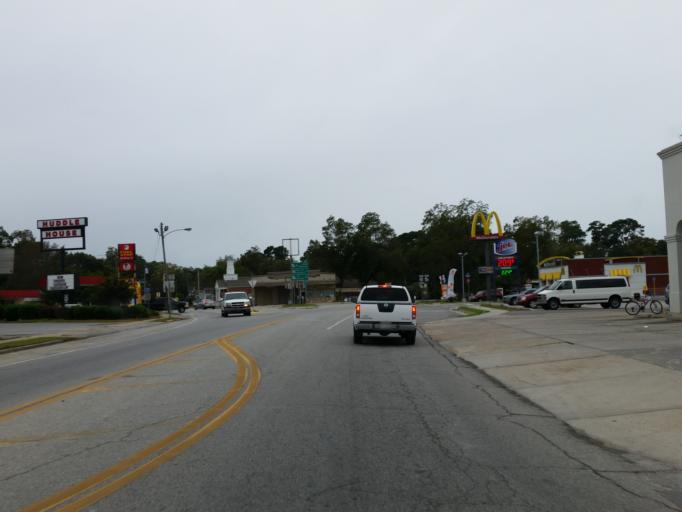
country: US
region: Georgia
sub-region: Lanier County
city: Lakeland
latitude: 31.0410
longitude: -83.0760
